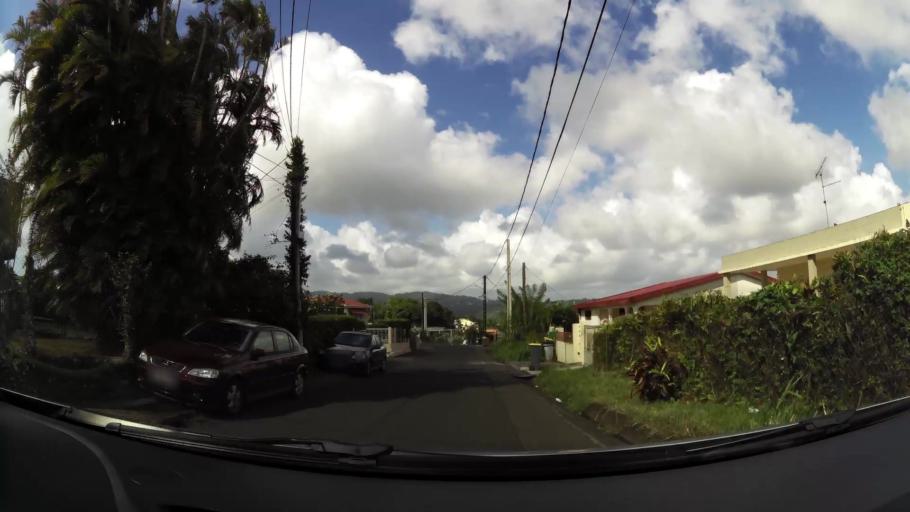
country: MQ
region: Martinique
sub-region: Martinique
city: Saint-Joseph
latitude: 14.6432
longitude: -61.0549
